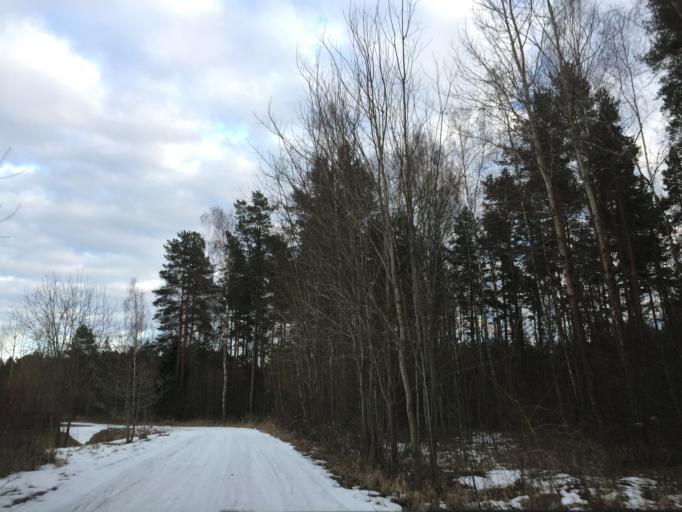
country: LV
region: Babite
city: Pinki
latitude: 56.9187
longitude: 23.8667
